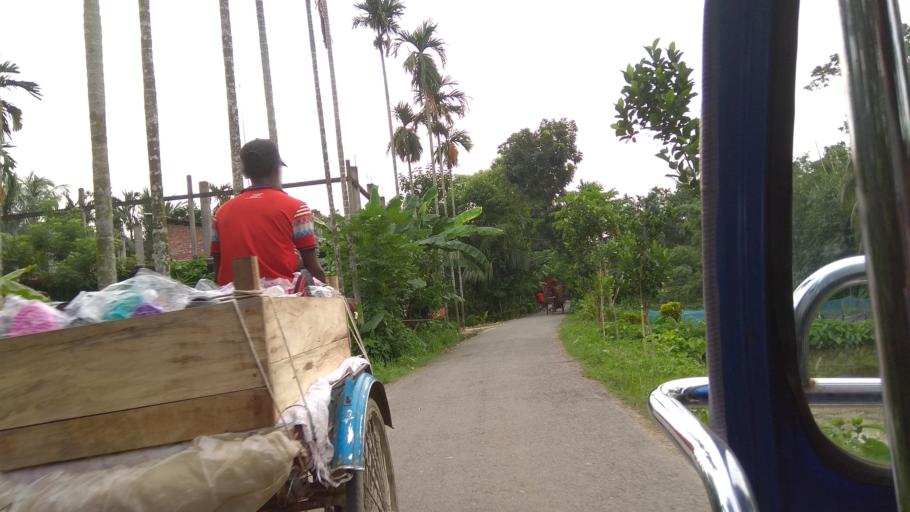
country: BD
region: Khulna
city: Kalia
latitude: 23.0306
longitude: 89.6510
